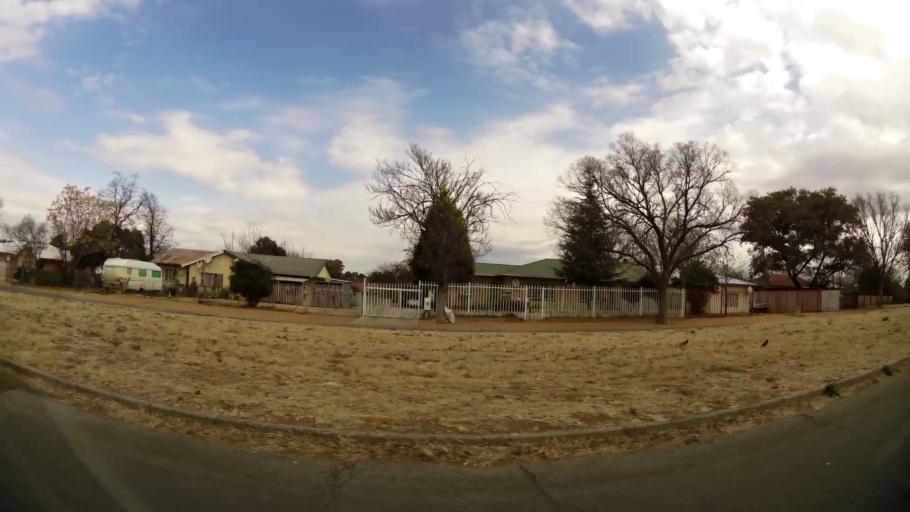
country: ZA
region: Orange Free State
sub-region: Fezile Dabi District Municipality
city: Kroonstad
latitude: -27.6442
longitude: 27.2281
